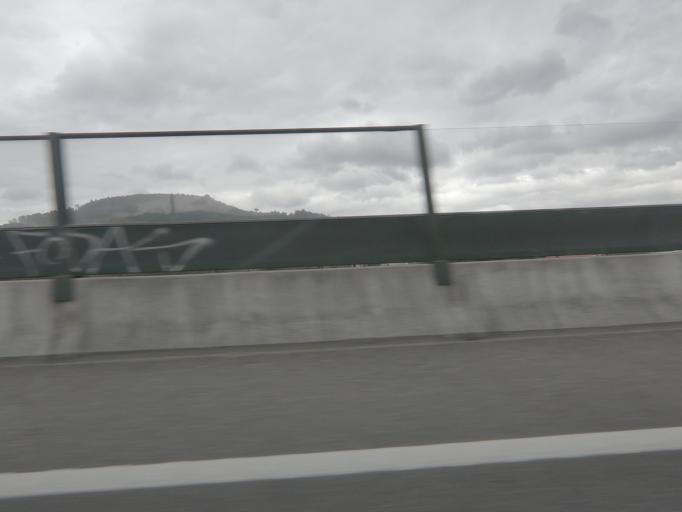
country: ES
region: Galicia
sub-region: Provincia de Ourense
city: Punxin
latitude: 42.3495
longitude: -7.9959
